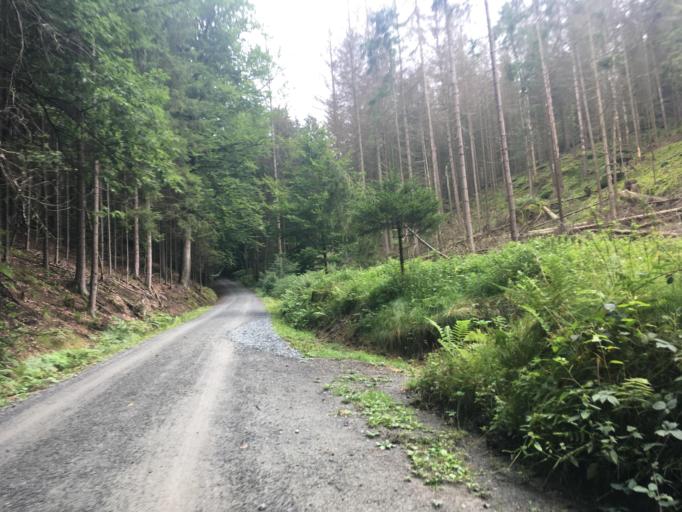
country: DE
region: Saxony
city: Bad Schandau
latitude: 50.9201
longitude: 14.1972
